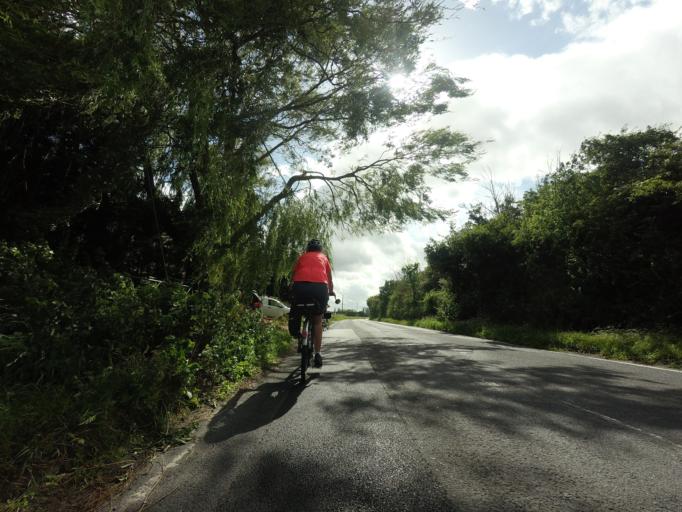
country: GB
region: England
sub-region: Medway
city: Stoke
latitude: 51.4621
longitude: 0.6117
